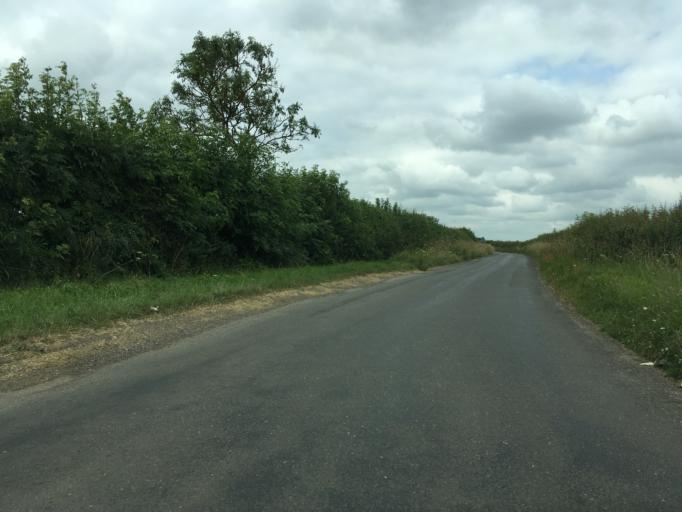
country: GB
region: England
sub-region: Oxfordshire
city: Charlbury
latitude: 51.9165
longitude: -1.4834
